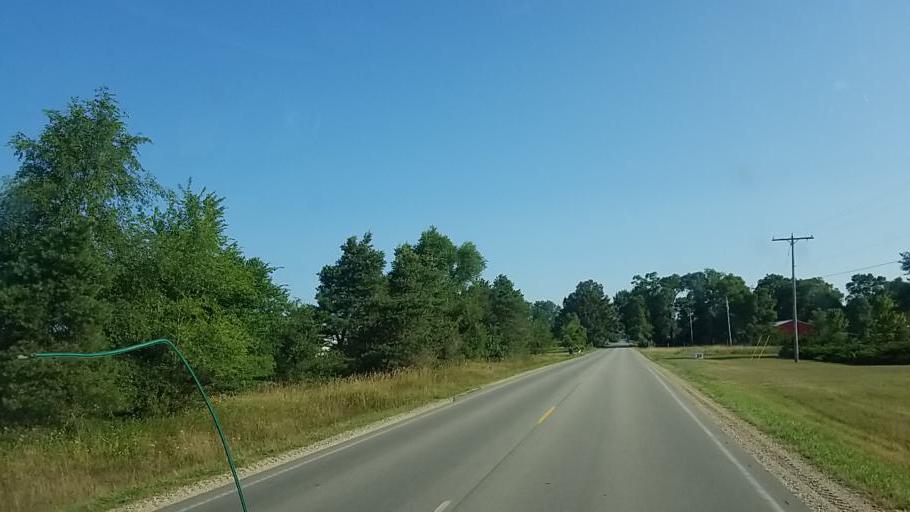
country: US
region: Michigan
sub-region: Newaygo County
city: Fremont
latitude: 43.4115
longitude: -85.9395
